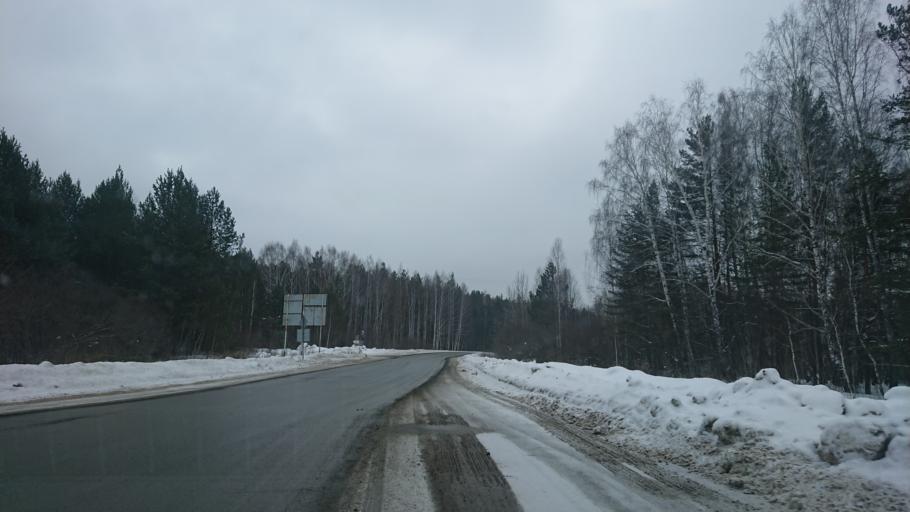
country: RU
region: Sverdlovsk
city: Sysert'
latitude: 56.4450
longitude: 60.8824
